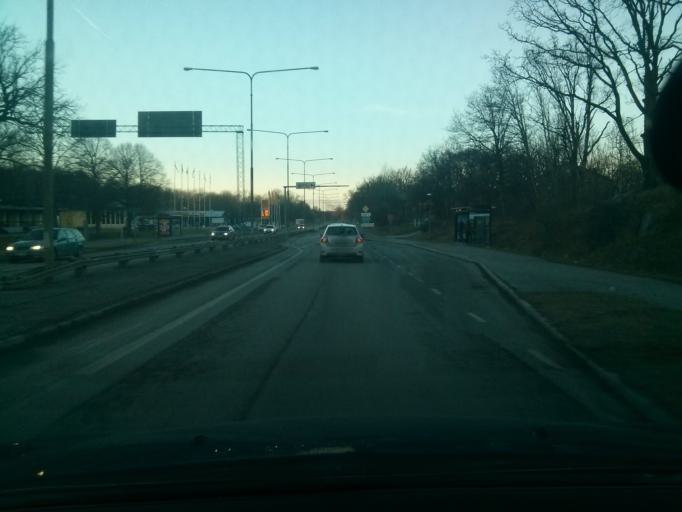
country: SE
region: Blekinge
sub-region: Karlskrona Kommun
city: Karlskrona
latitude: 56.1962
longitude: 15.6121
